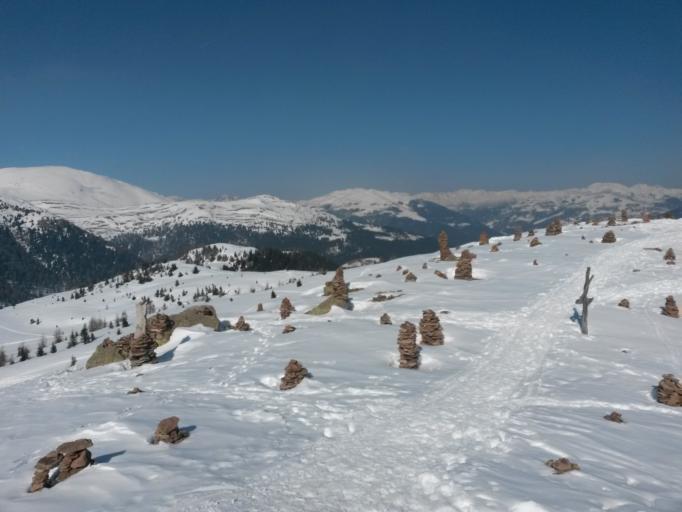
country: IT
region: Trentino-Alto Adige
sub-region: Bolzano
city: Sarentino
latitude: 46.6355
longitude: 11.3039
